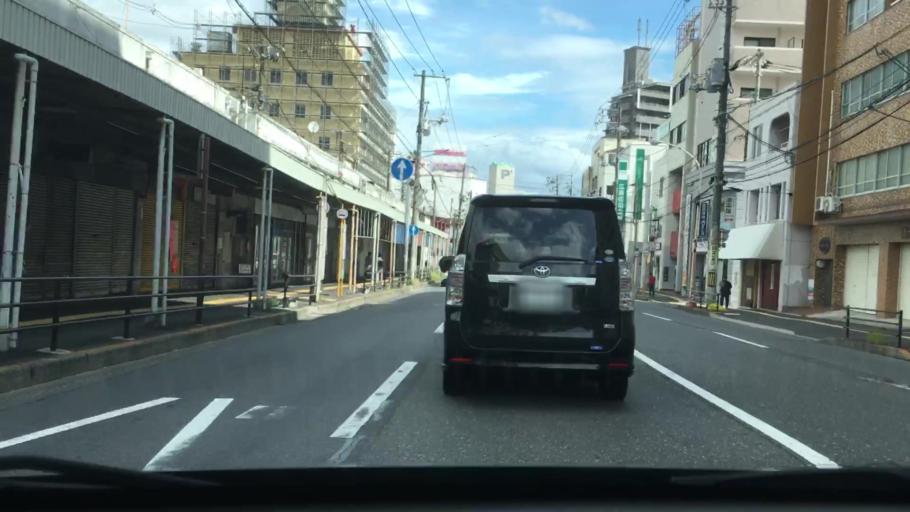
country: JP
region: Hiroshima
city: Hiroshima-shi
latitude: 34.3964
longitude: 132.4275
